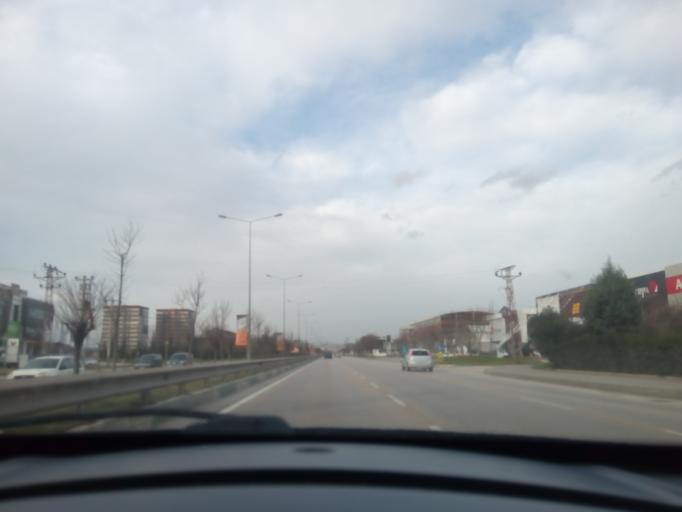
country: TR
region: Bursa
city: Cali
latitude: 40.2127
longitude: 28.9284
